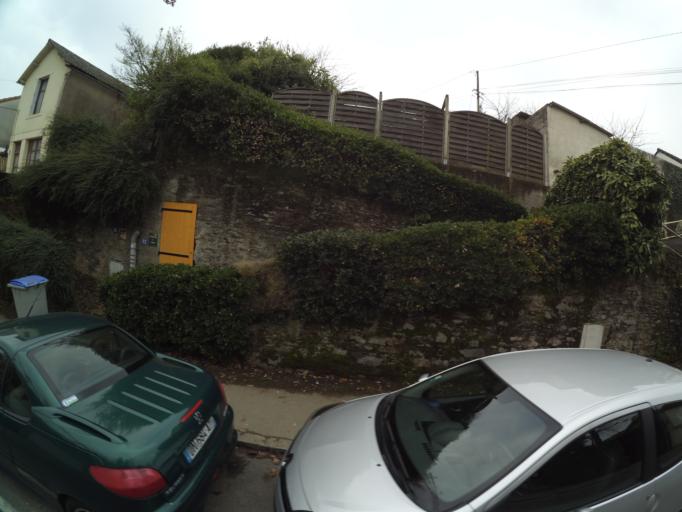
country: FR
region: Pays de la Loire
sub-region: Departement de la Loire-Atlantique
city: Nantes
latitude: 47.2408
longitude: -1.5564
